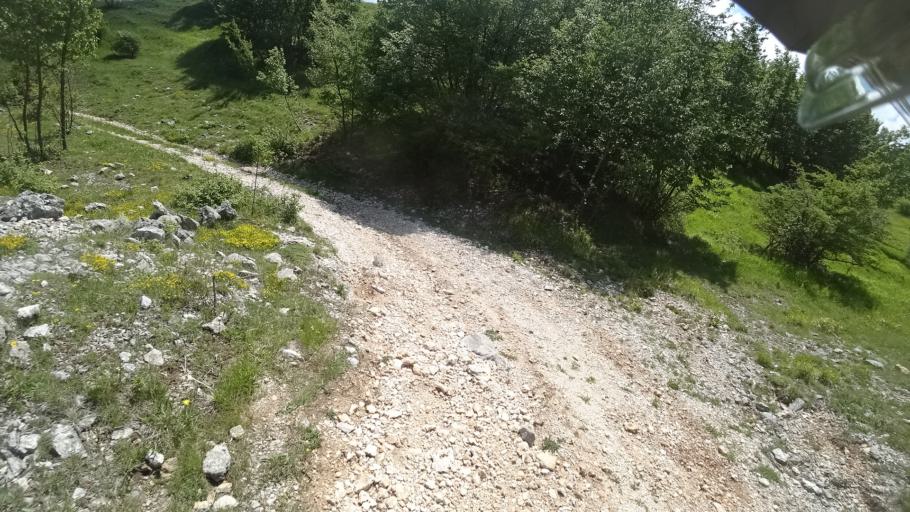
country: HR
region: Zadarska
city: Gracac
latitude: 44.3696
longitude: 15.9532
